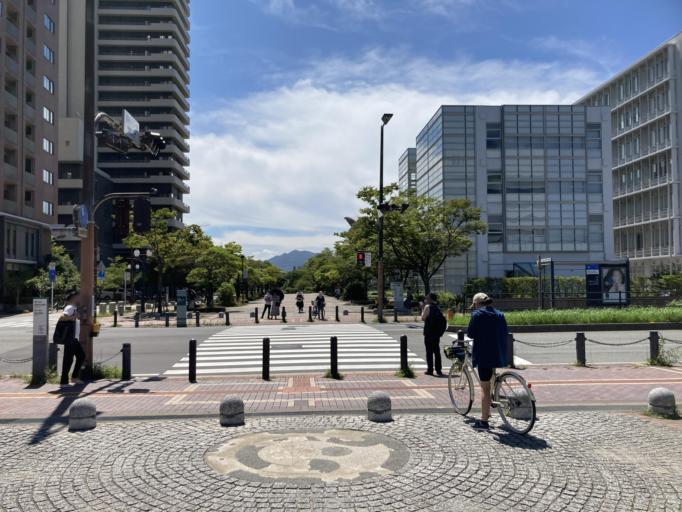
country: JP
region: Fukuoka
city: Fukuoka-shi
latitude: 33.5920
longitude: 130.3517
